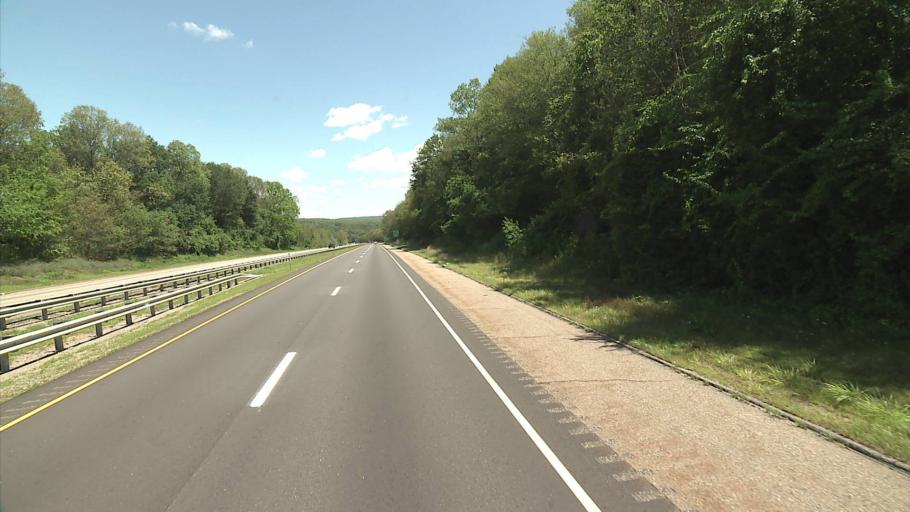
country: US
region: Connecticut
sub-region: New London County
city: Jewett City
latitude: 41.6026
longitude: -71.9554
